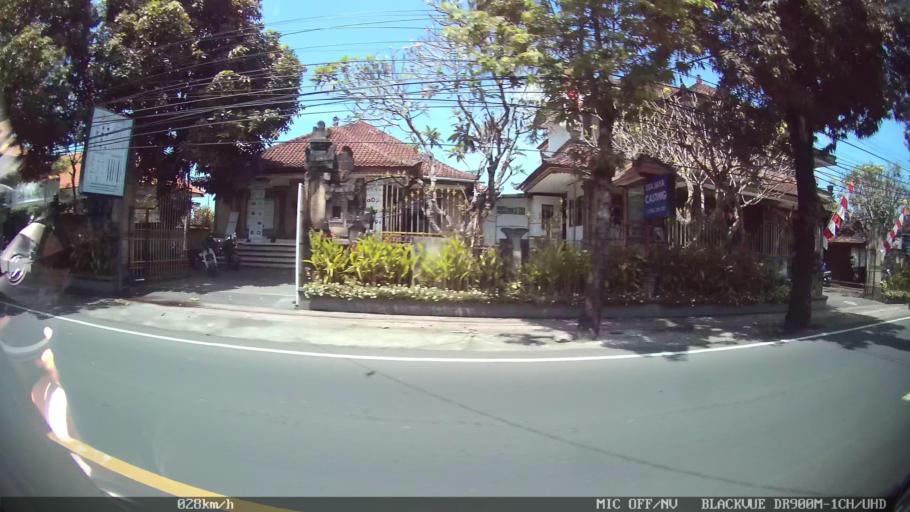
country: ID
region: Bali
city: Banjar Jabejero
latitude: -8.6006
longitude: 115.2687
